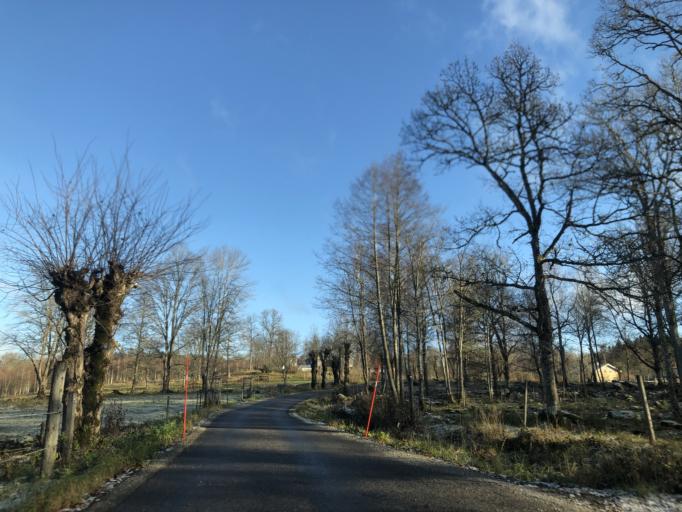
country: SE
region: Vaestra Goetaland
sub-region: Ulricehamns Kommun
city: Ulricehamn
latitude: 57.7246
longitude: 13.4083
